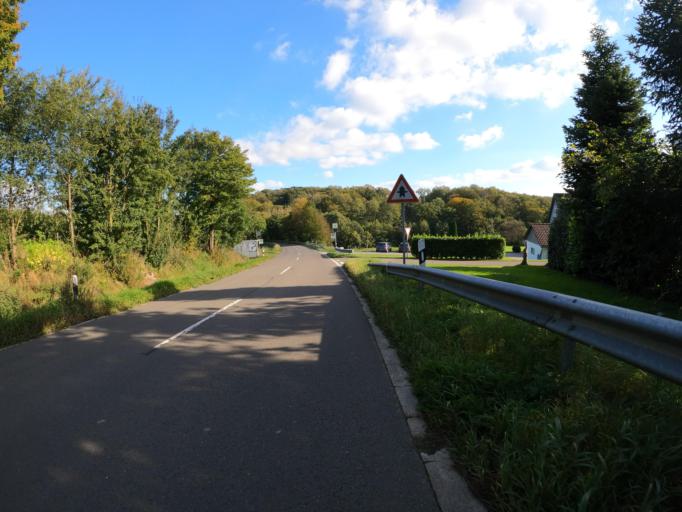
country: DE
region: North Rhine-Westphalia
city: Radevormwald
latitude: 51.2270
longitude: 7.3439
